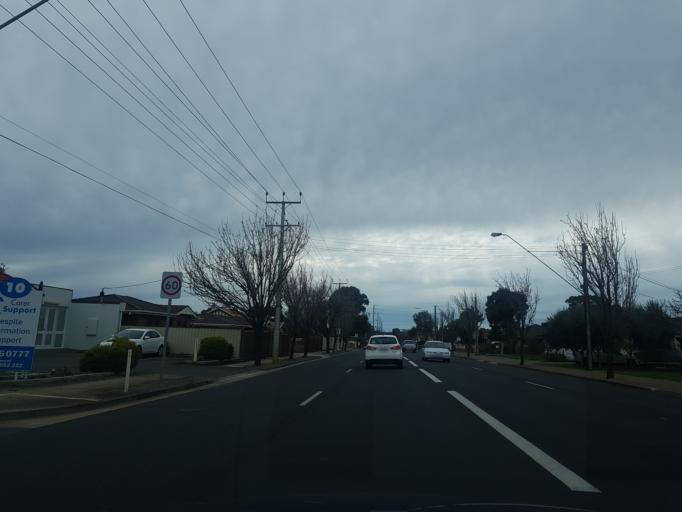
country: AU
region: South Australia
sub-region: Campbelltown
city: Campbelltown
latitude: -34.8872
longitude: 138.6741
